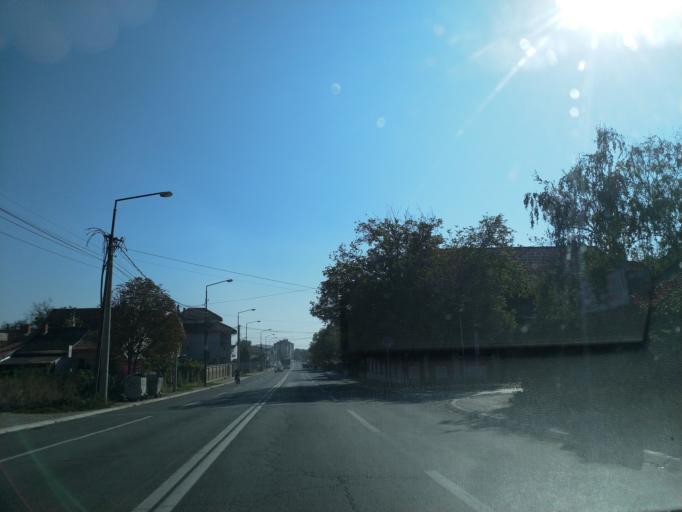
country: RS
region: Central Serbia
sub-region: Pomoravski Okrug
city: Paracin
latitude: 43.8652
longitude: 21.4206
